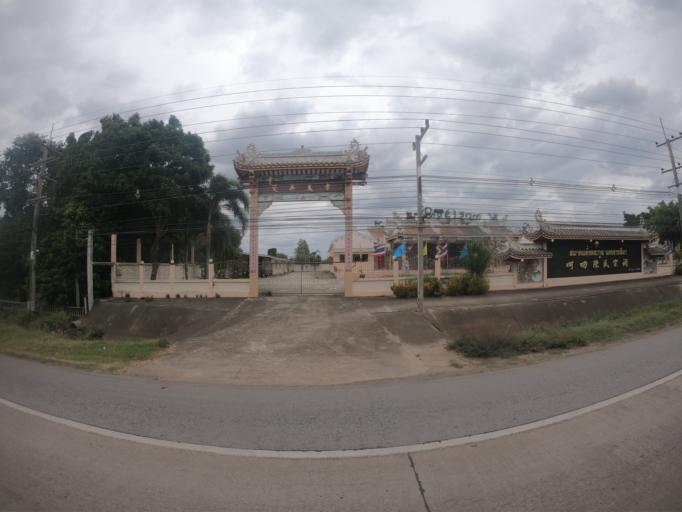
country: TH
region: Nakhon Ratchasima
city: Chok Chai
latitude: 14.7805
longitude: 102.1636
